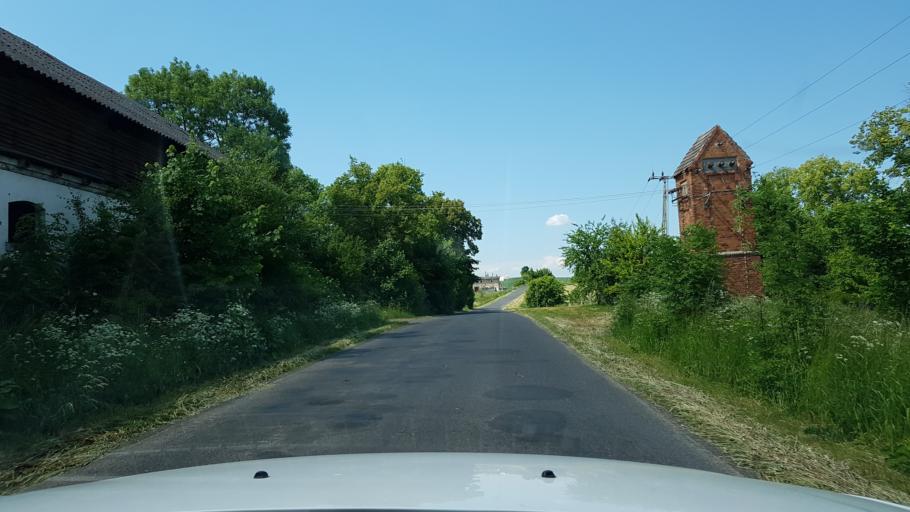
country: PL
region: West Pomeranian Voivodeship
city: Trzcinsko Zdroj
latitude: 52.9991
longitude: 14.5712
